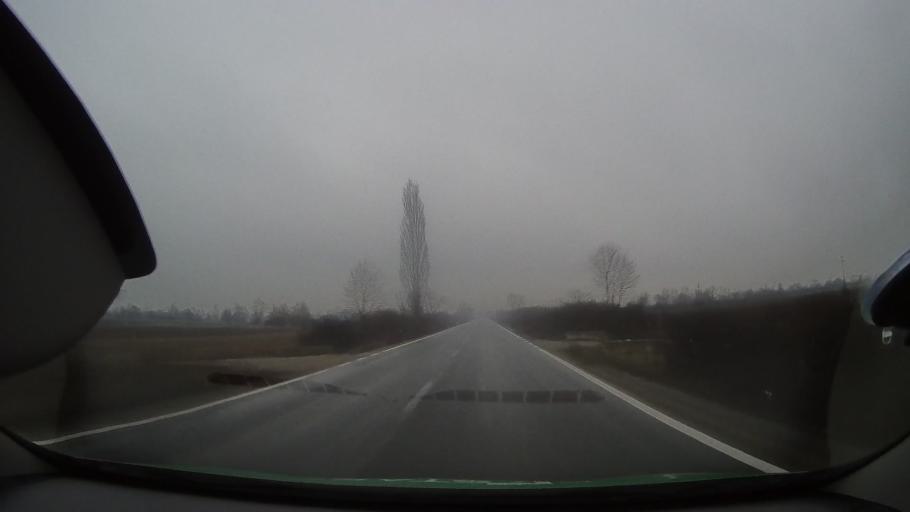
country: RO
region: Bihor
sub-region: Comuna Tinca
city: Tinca
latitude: 46.7478
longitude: 21.9382
